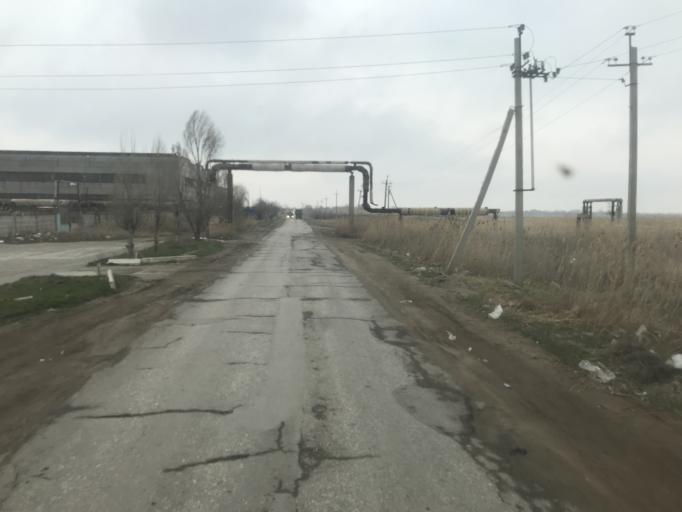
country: RU
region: Volgograd
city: Svetlyy Yar
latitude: 48.5254
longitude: 44.6158
